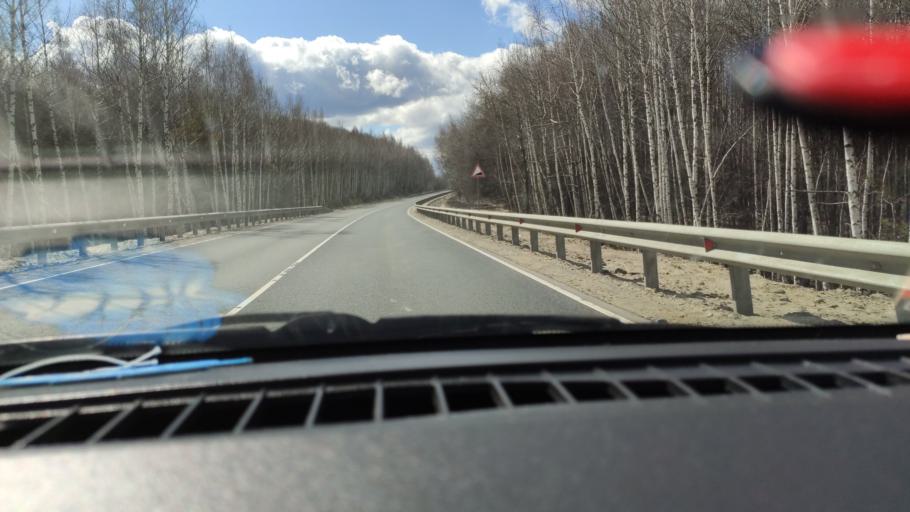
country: RU
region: Saratov
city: Khvalynsk
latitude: 52.4546
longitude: 48.0146
